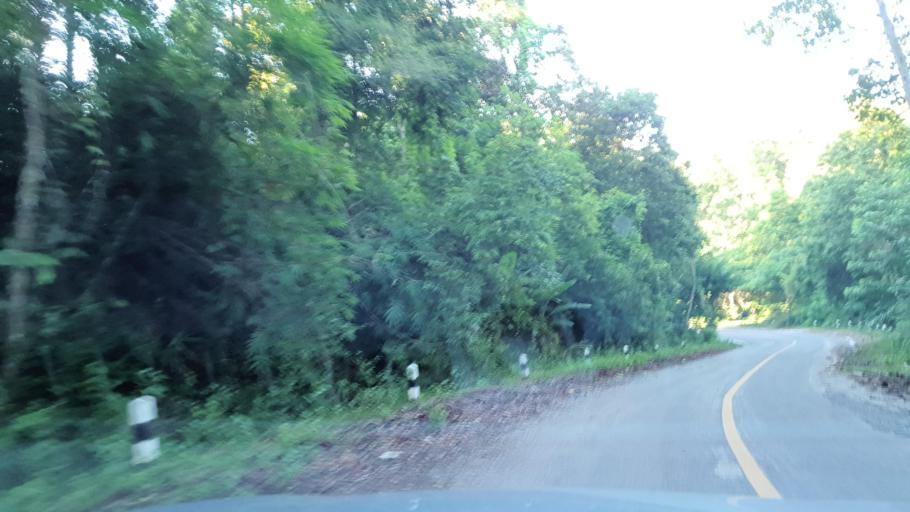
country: TH
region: Chiang Mai
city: Mae On
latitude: 18.8105
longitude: 99.2996
